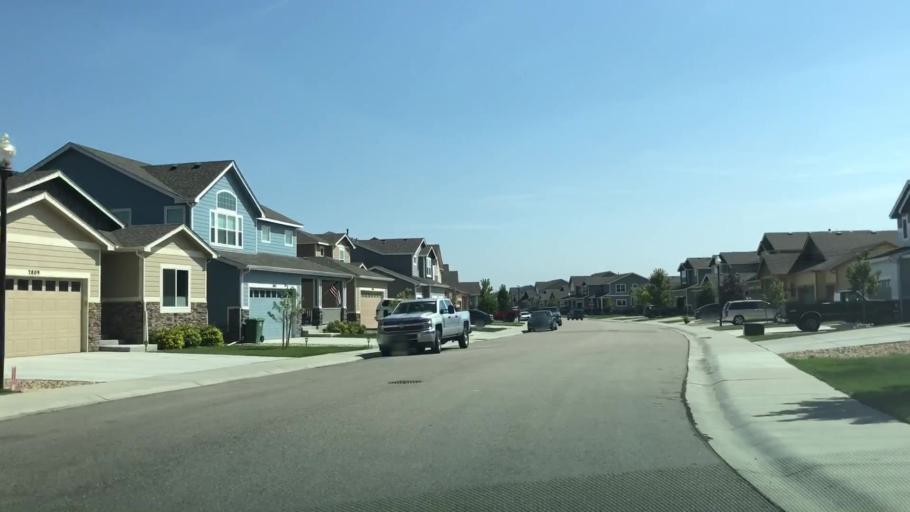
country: US
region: Colorado
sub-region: Larimer County
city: Loveland
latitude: 40.4035
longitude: -105.0358
